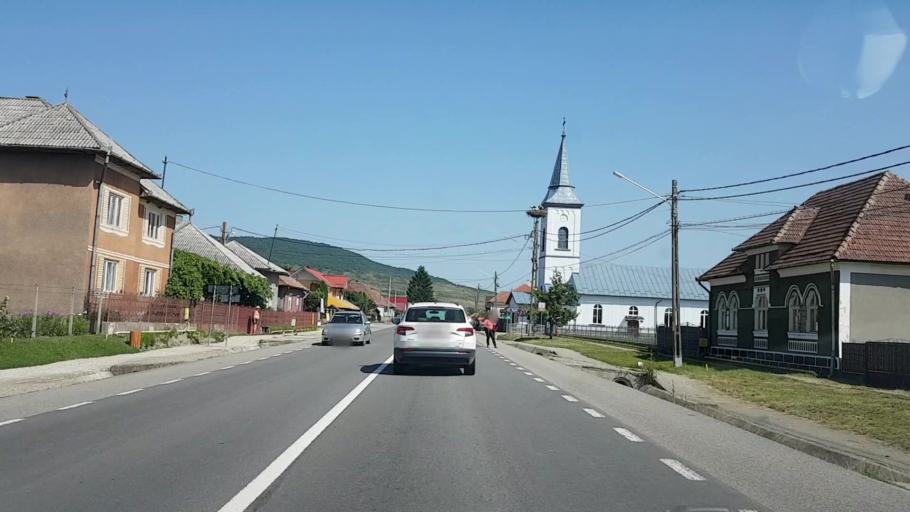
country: RO
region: Bistrita-Nasaud
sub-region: Comuna Sieu-Magherus
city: Sieu-Magherus
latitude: 47.0898
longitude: 24.3754
